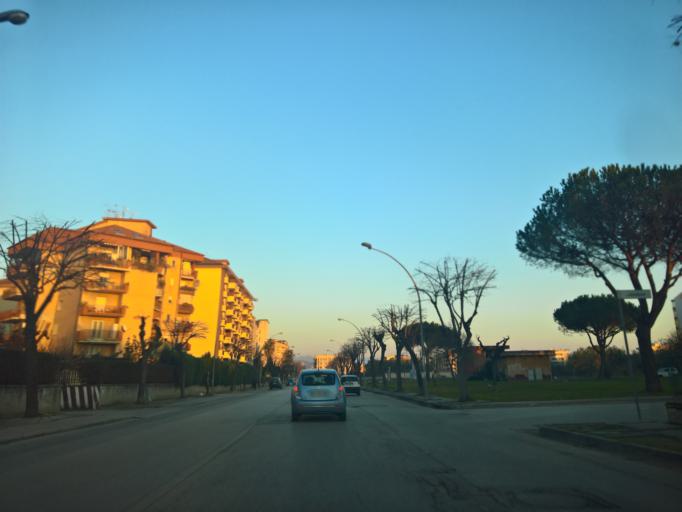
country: IT
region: Campania
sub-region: Provincia di Caserta
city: Santa Maria Capua Vetere
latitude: 41.0899
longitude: 14.2616
